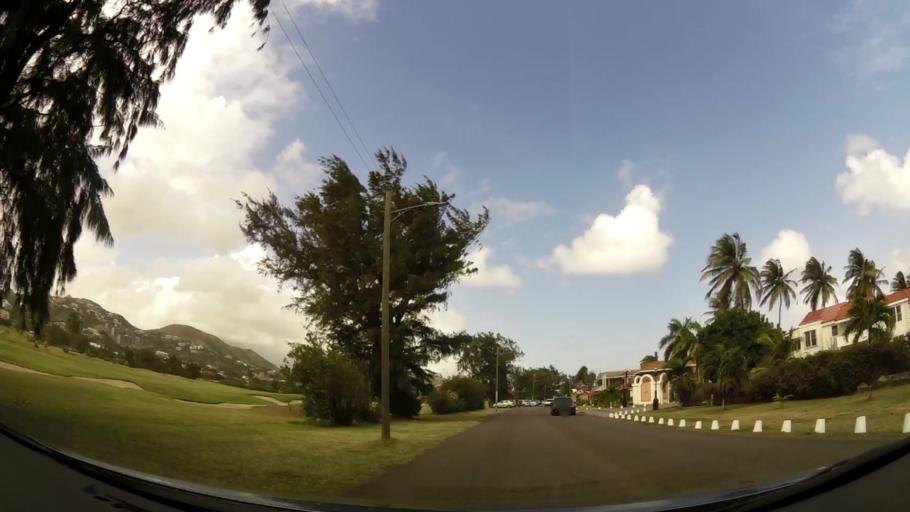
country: KN
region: Saint George Basseterre
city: Basseterre
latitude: 17.2855
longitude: -62.6854
